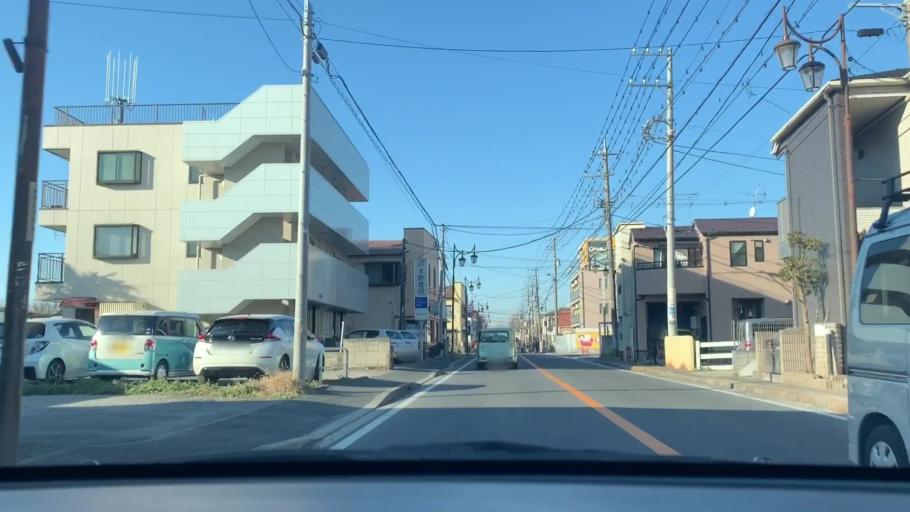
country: JP
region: Chiba
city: Matsudo
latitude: 35.7497
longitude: 139.9033
